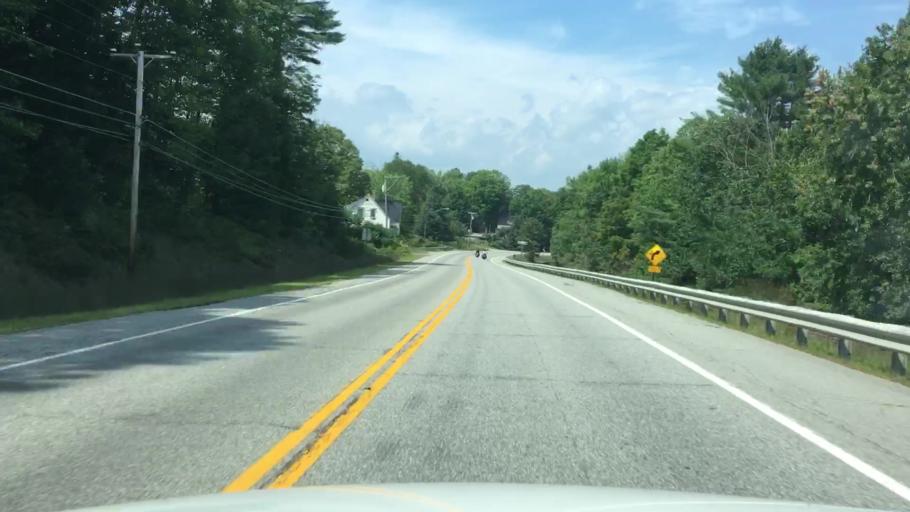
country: US
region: Maine
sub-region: Oxford County
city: Peru
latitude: 44.5049
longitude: -70.4030
